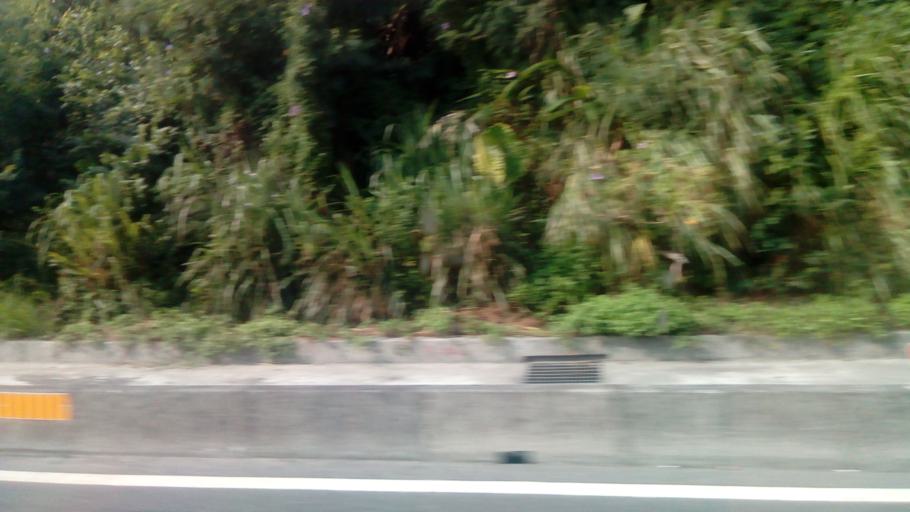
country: TW
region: Taiwan
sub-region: Yilan
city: Yilan
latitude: 24.5956
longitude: 121.8578
